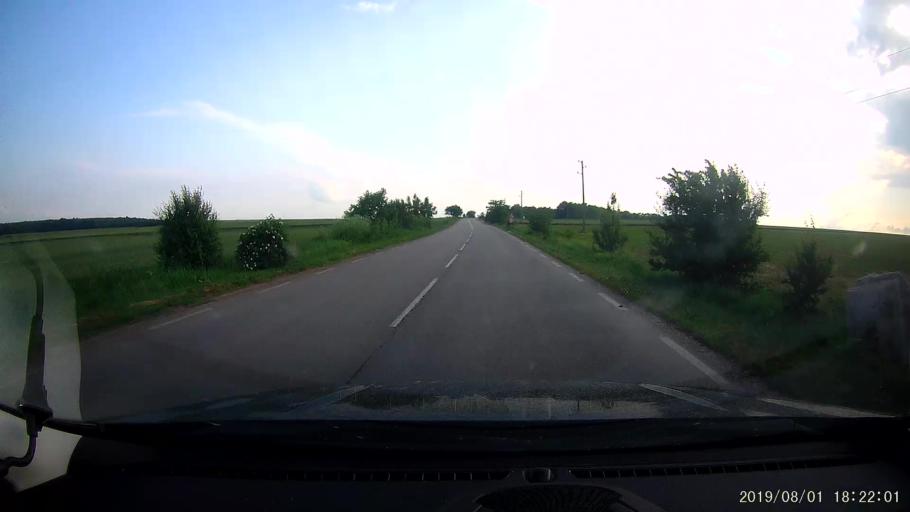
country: BG
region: Shumen
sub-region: Obshtina Kaolinovo
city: Kaolinovo
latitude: 43.6435
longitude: 27.0605
